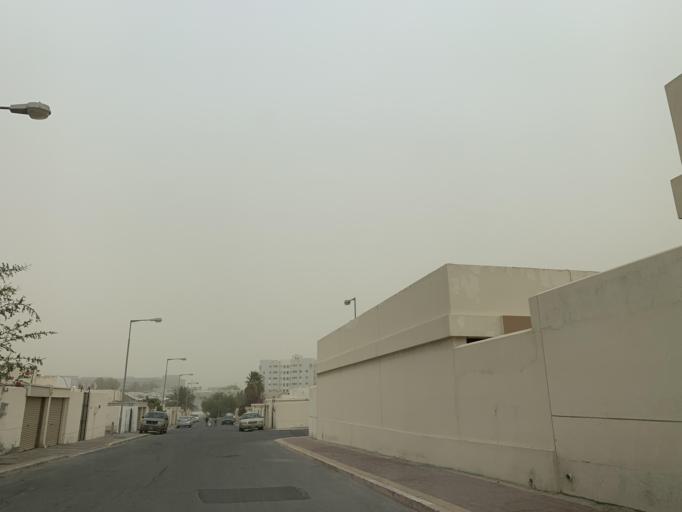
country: BH
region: Central Governorate
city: Madinat Hamad
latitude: 26.1336
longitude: 50.5198
